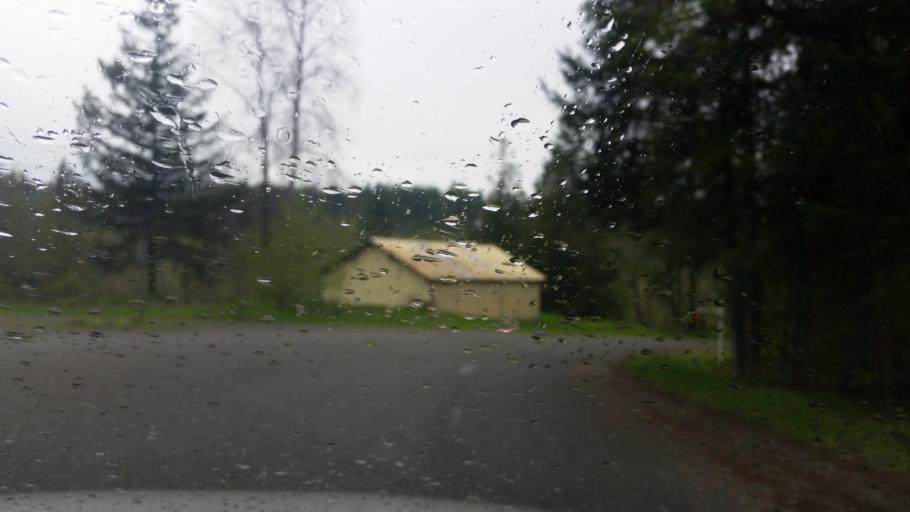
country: US
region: Washington
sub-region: Pierce County
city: Eatonville
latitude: 46.8661
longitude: -122.3400
